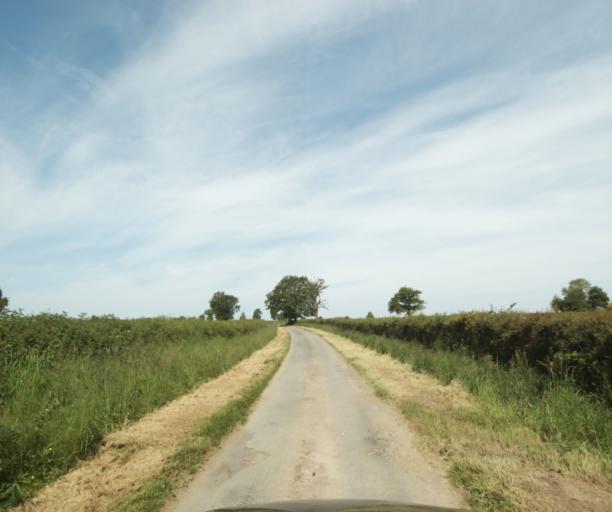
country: FR
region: Bourgogne
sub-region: Departement de Saone-et-Loire
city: Palinges
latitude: 46.5624
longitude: 4.1727
